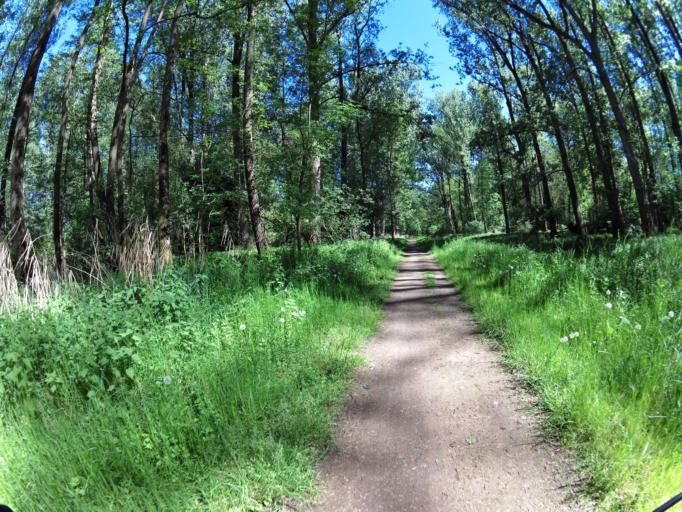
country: DE
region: North Rhine-Westphalia
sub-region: Regierungsbezirk Koln
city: Selfkant
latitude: 50.9950
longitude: 5.9355
